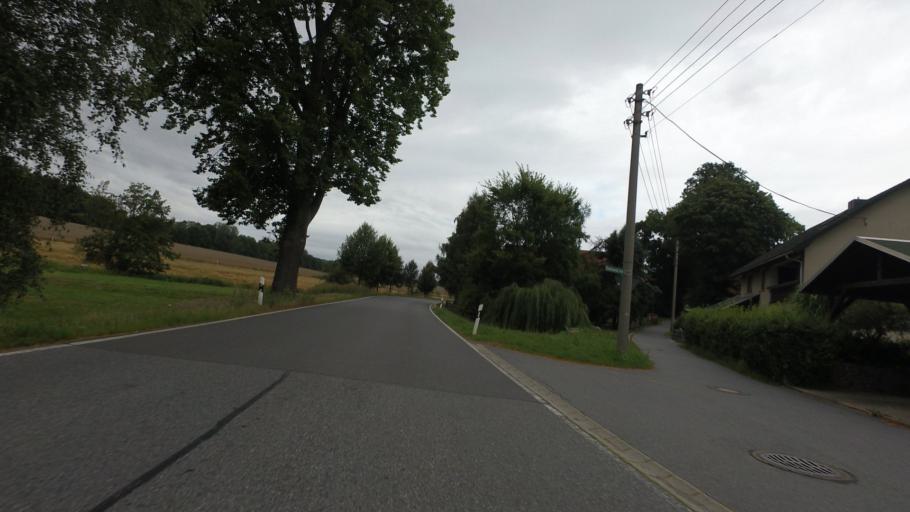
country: DE
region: Saxony
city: Berthelsdorf
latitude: 51.0402
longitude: 14.2194
